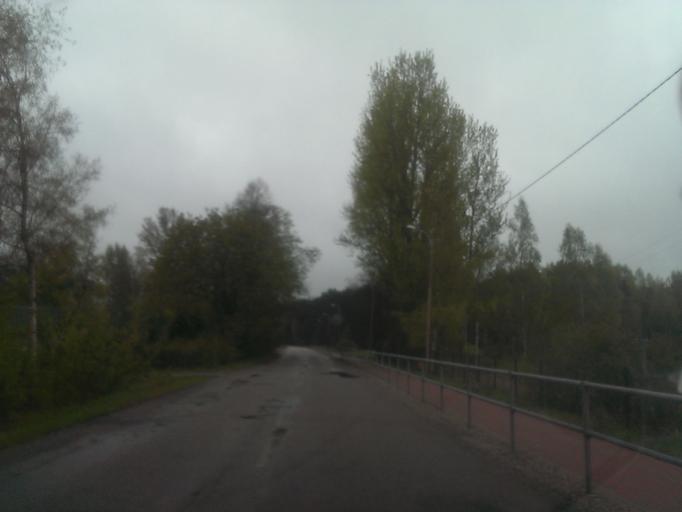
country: LV
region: Ventspils
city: Ventspils
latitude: 57.4369
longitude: 21.6226
